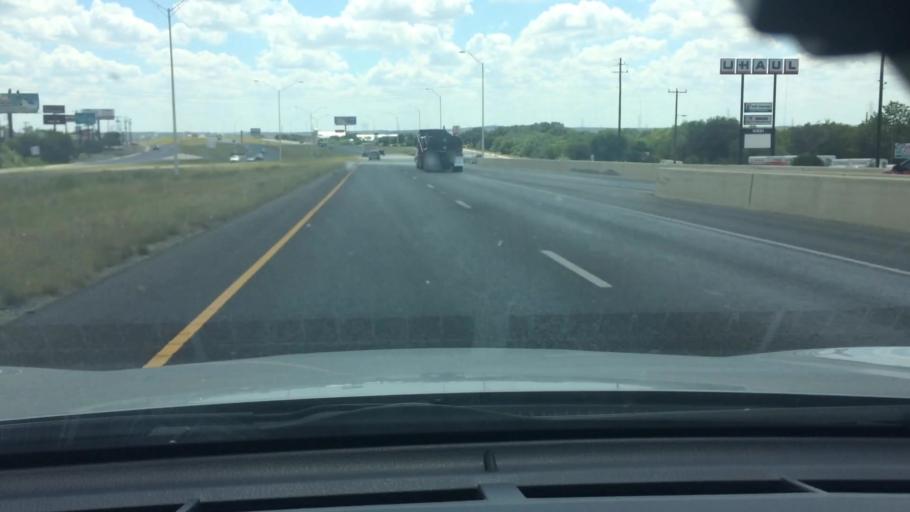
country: US
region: Texas
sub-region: Bexar County
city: Helotes
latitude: 29.5422
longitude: -98.6787
